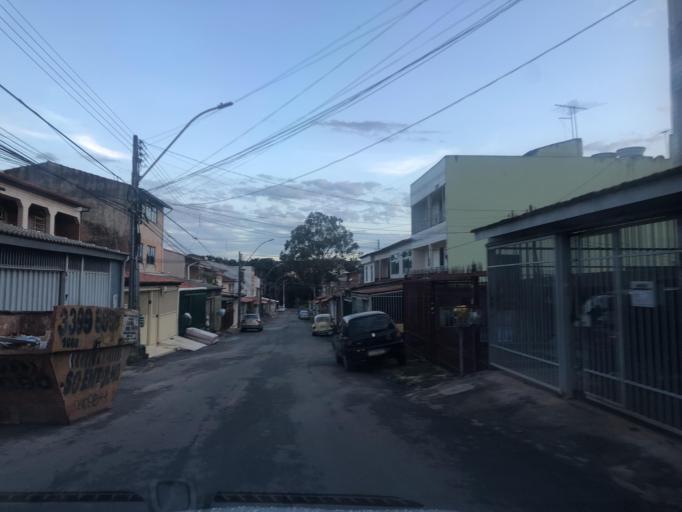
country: BR
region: Federal District
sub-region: Brasilia
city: Brasilia
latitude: -15.8775
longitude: -47.9787
